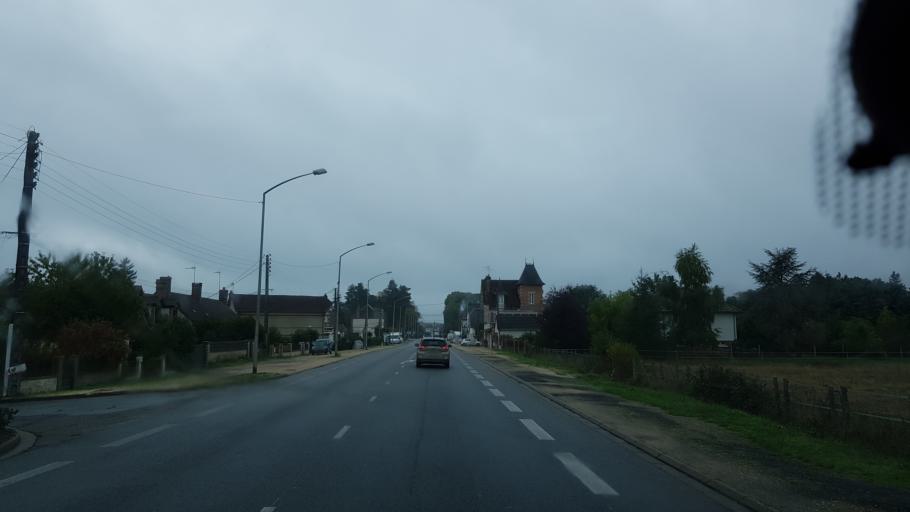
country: FR
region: Centre
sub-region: Departement du Loir-et-Cher
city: Salbris
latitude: 47.4341
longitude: 2.0494
